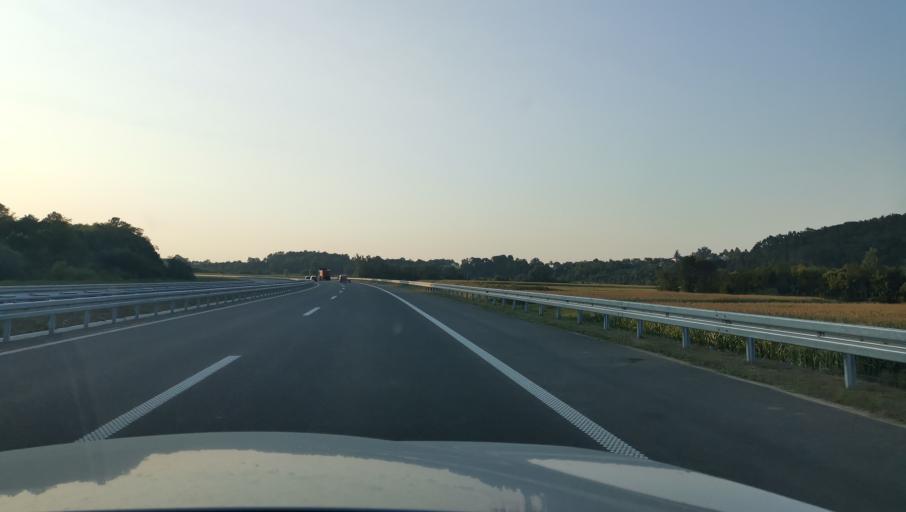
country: RS
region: Central Serbia
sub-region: Kolubarski Okrug
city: Lajkovac
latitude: 44.3395
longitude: 20.1975
